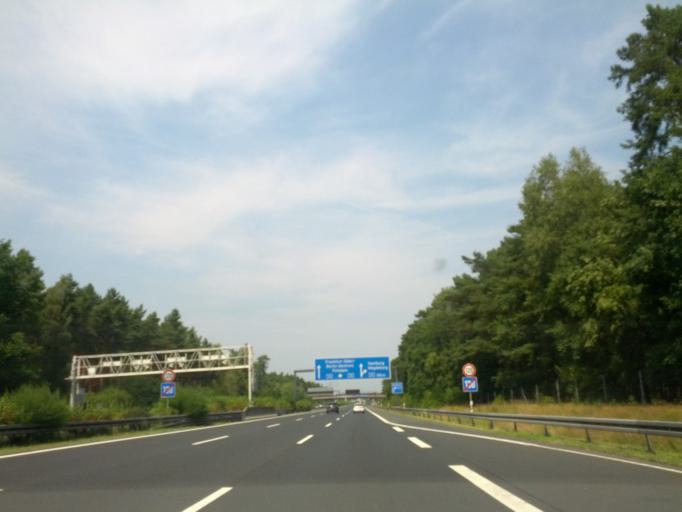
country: DE
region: Brandenburg
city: Fichtenwalde
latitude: 52.2736
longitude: 12.9109
